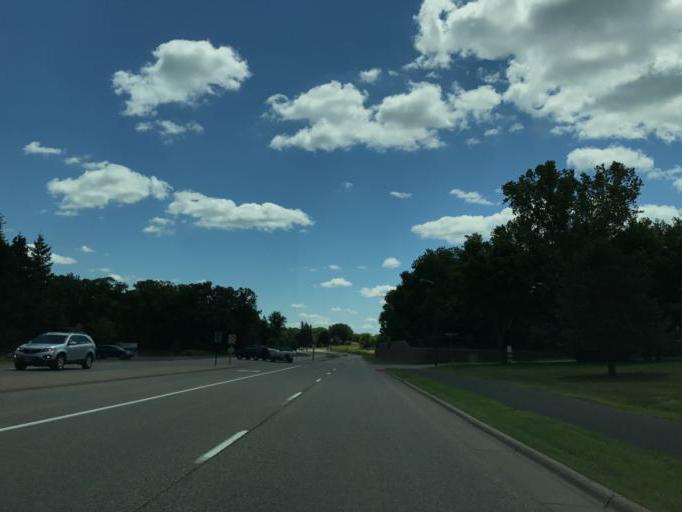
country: US
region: Minnesota
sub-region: Hennepin County
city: Maple Grove
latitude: 45.0780
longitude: -93.4714
